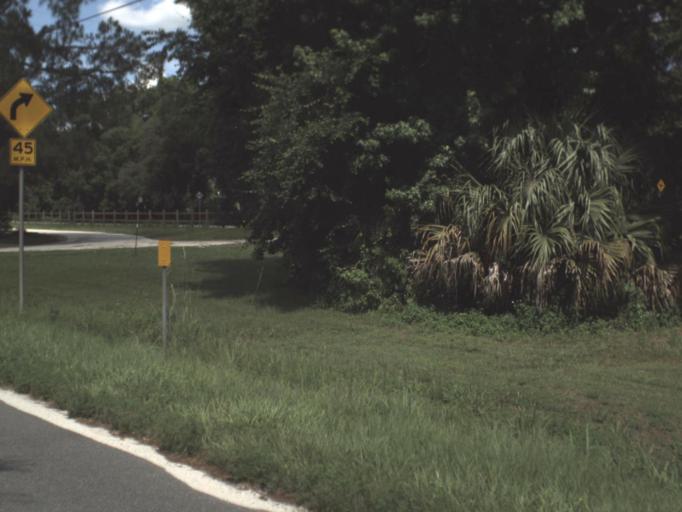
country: US
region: Florida
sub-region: Putnam County
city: Interlachen
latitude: 29.7288
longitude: -81.9156
